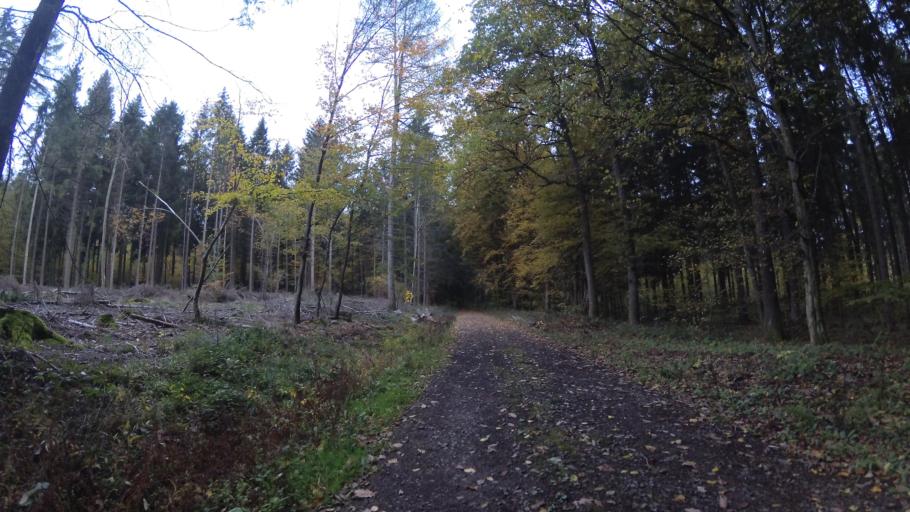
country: DE
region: Saarland
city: Sankt Wendel
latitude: 49.4528
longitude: 7.2033
